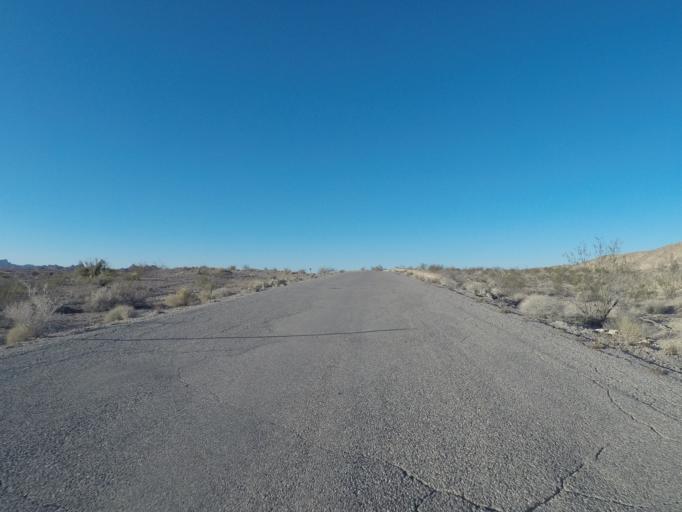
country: US
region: Nevada
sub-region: Clark County
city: Moapa Valley
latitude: 36.3925
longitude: -114.4229
